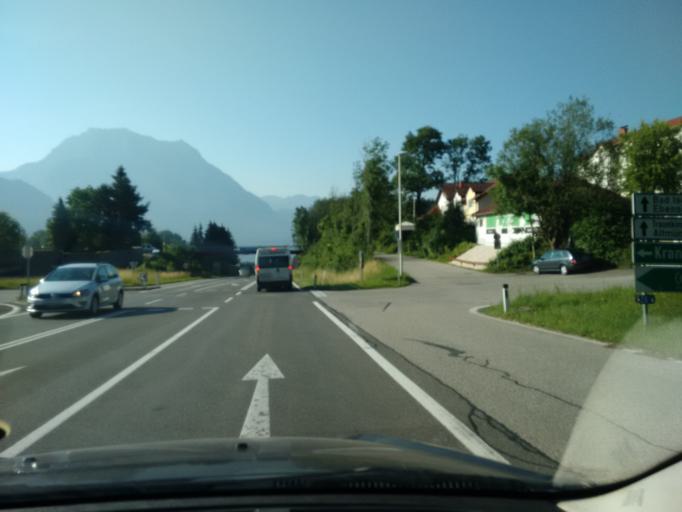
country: AT
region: Upper Austria
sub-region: Politischer Bezirk Gmunden
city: Altmunster
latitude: 47.9134
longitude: 13.7775
